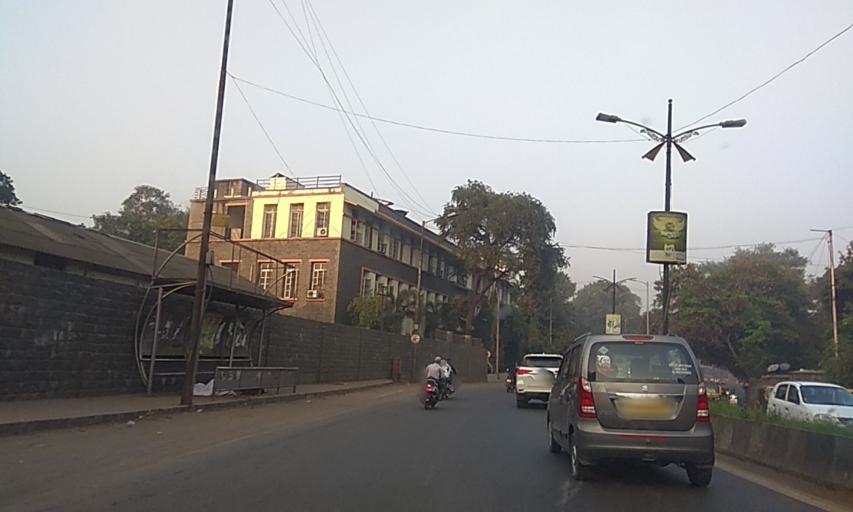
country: IN
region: Maharashtra
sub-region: Pune Division
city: Shivaji Nagar
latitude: 18.5294
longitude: 73.8586
